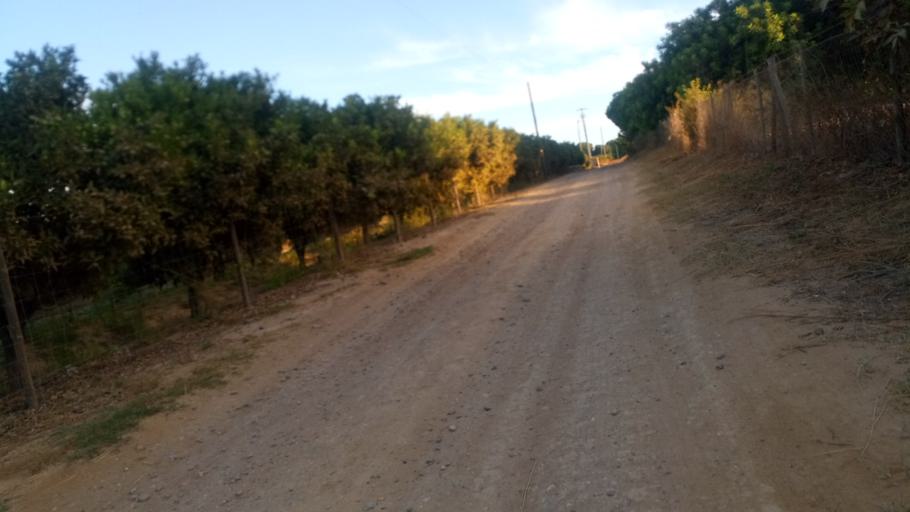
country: PT
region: Faro
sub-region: Tavira
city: Tavira
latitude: 37.1488
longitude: -7.5865
